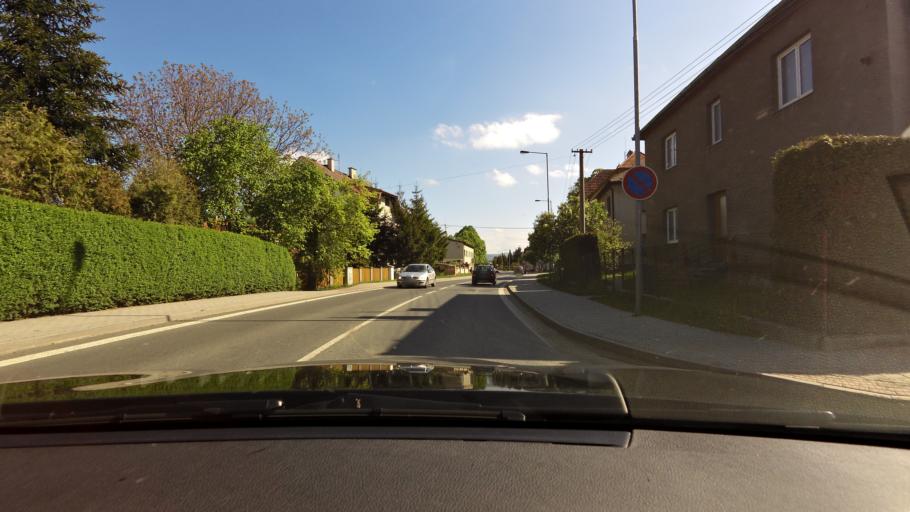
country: CZ
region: Plzensky
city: Klatovy
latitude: 49.3763
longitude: 13.3003
